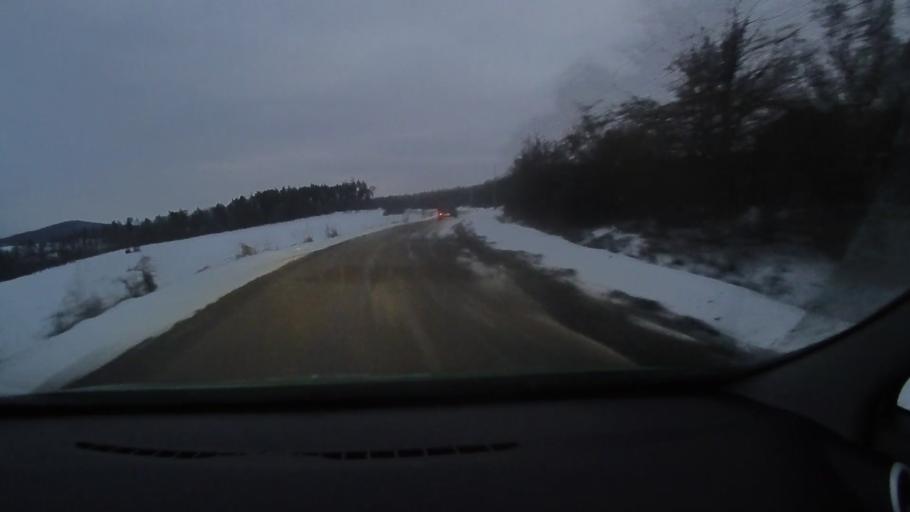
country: RO
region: Harghita
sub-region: Comuna Darjiu
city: Darjiu
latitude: 46.1861
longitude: 25.2473
